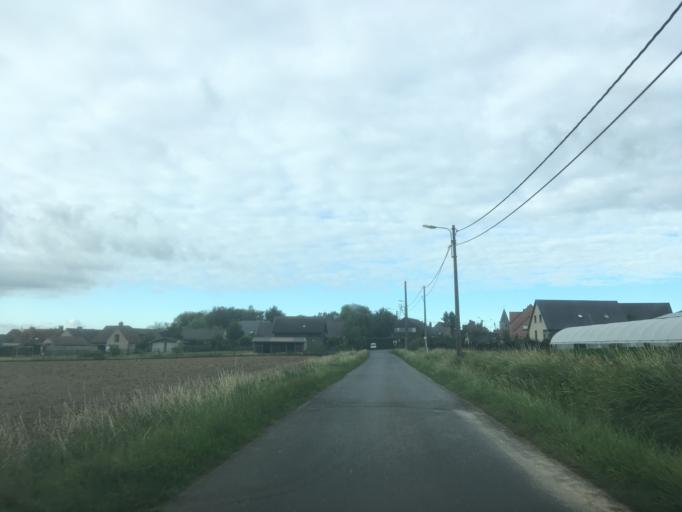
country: BE
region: Flanders
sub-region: Provincie West-Vlaanderen
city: Ardooie
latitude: 51.0045
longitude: 3.2152
